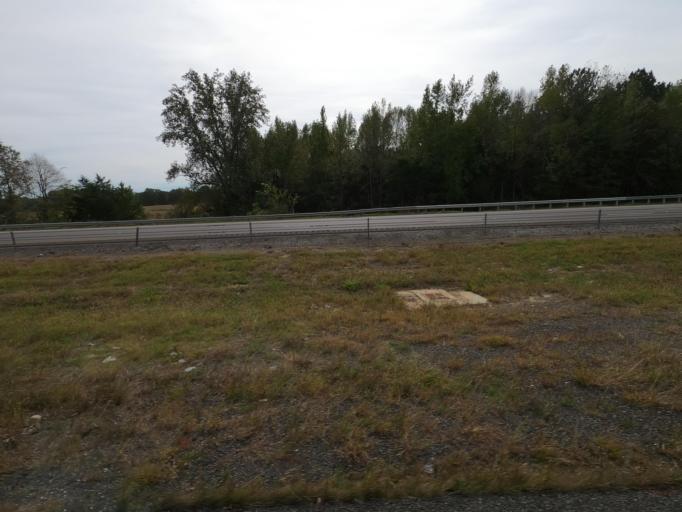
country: US
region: Tennessee
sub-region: Henderson County
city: Lexington
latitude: 35.7552
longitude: -88.5101
